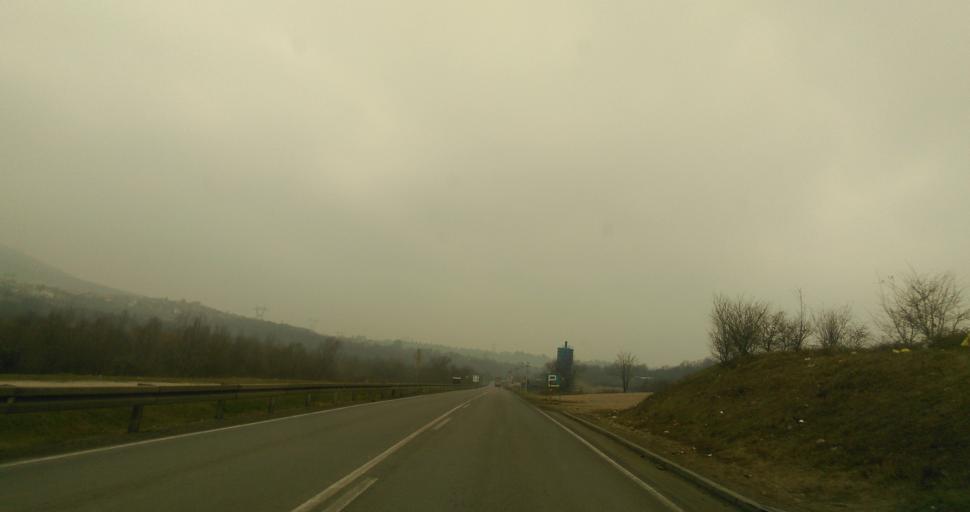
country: RS
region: Central Serbia
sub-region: Belgrade
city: Zvezdara
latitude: 44.7185
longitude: 20.5373
